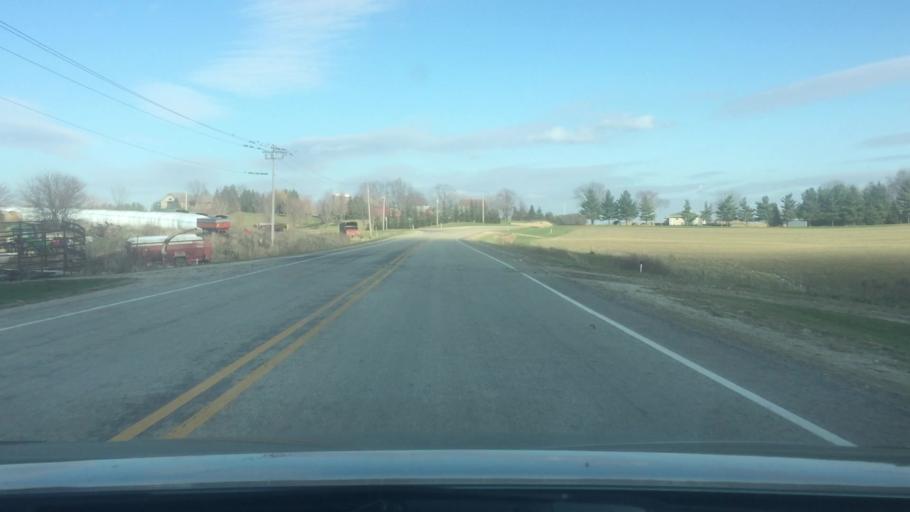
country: US
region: Wisconsin
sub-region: Jefferson County
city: Palmyra
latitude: 42.9316
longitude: -88.6770
